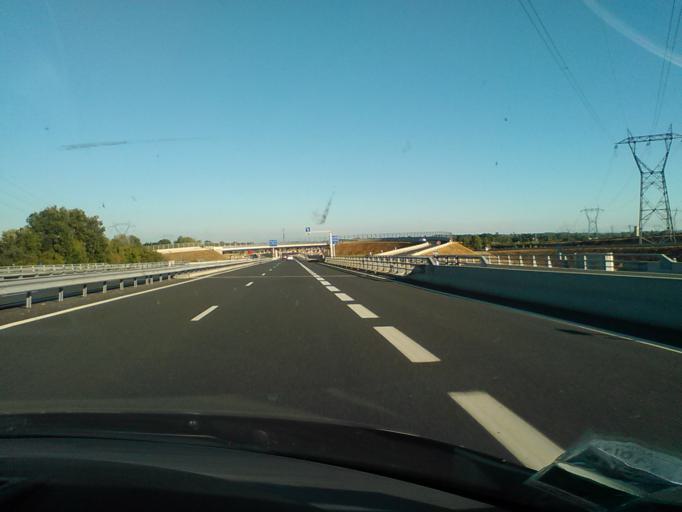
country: FR
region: Rhone-Alpes
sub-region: Departement de l'Ain
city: La Boisse
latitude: 45.8328
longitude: 5.0258
